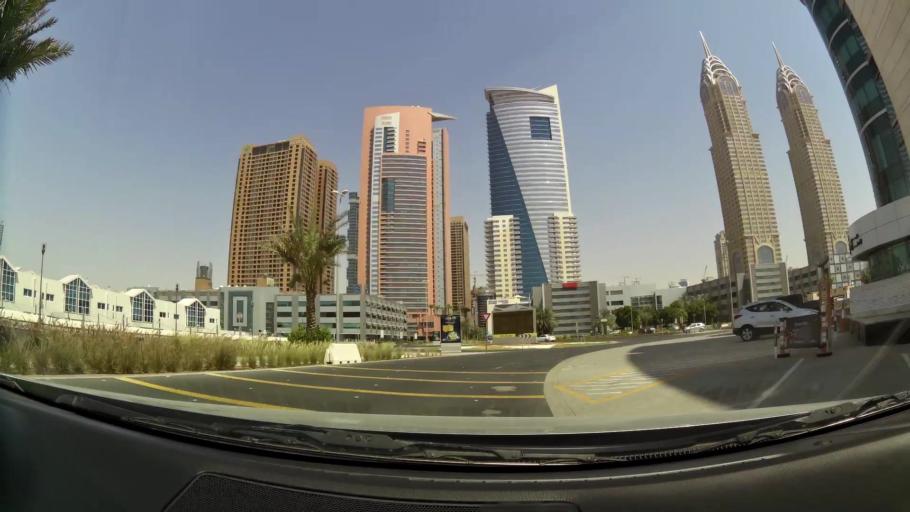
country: AE
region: Dubai
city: Dubai
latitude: 25.1039
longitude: 55.1689
